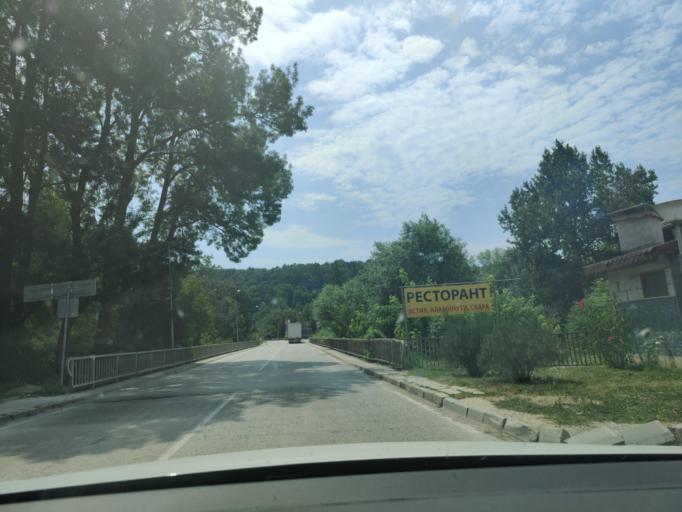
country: BG
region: Vidin
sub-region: Obshtina Dimovo
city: Dimovo
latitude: 43.7388
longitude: 22.7250
